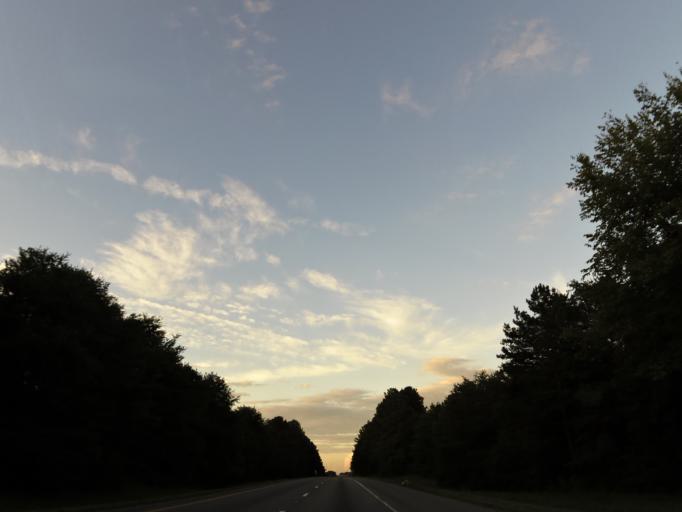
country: US
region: Tennessee
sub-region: McMinn County
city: Athens
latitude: 35.4952
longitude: -84.6190
